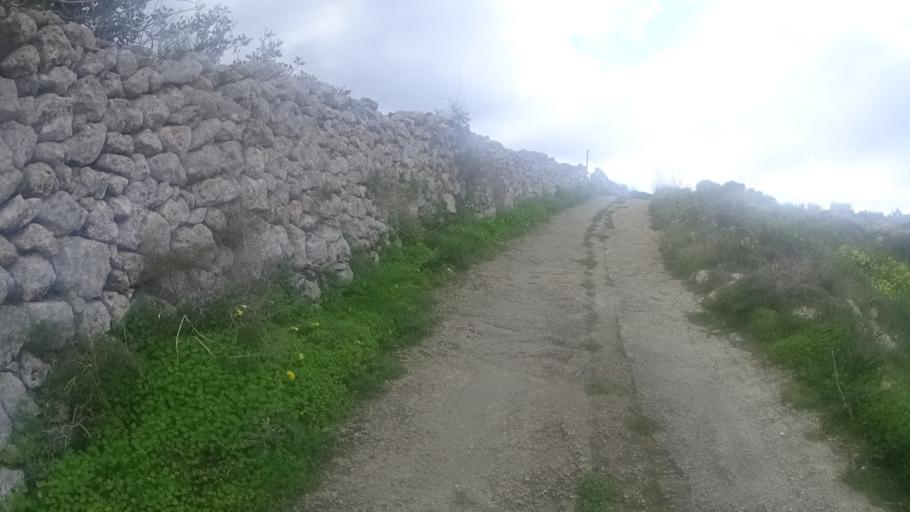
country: MT
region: L-Imtarfa
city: Imtarfa
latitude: 35.8947
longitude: 14.3739
